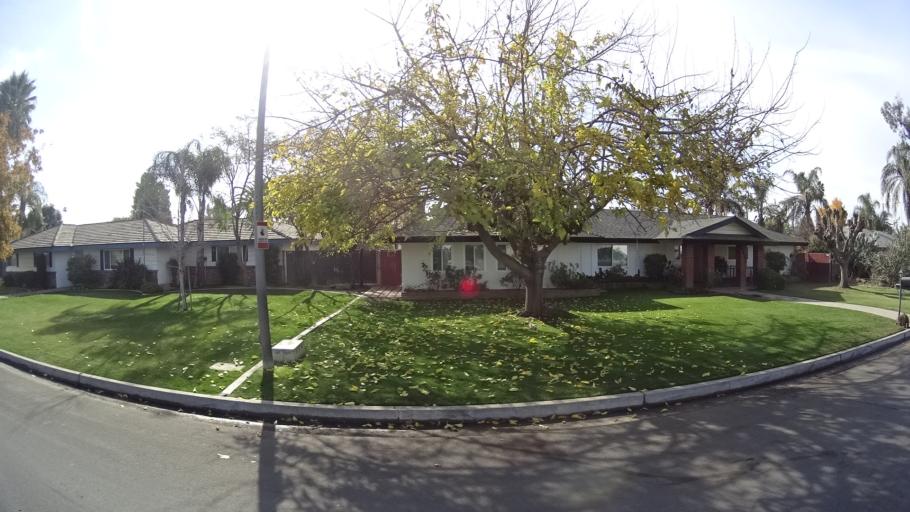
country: US
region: California
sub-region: Kern County
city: Greenacres
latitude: 35.4123
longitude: -119.0694
